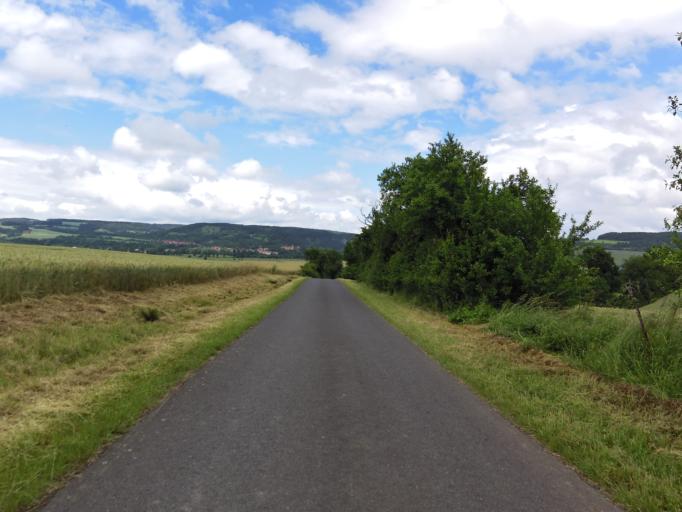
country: DE
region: Thuringia
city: Creuzburg
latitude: 51.0301
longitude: 10.2403
